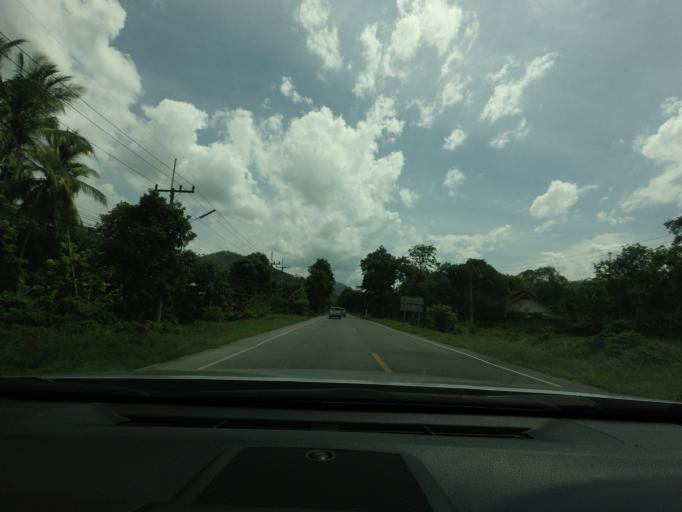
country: TH
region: Yala
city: Raman
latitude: 6.4544
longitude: 101.3513
